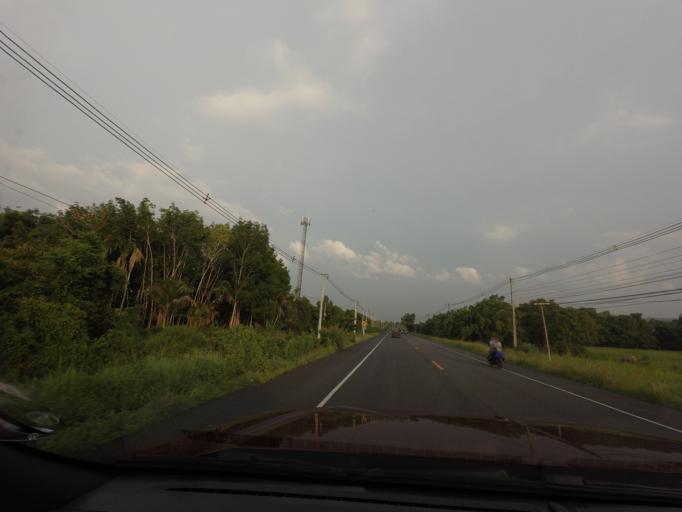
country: TH
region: Pattani
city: Mae Lan
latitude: 6.6447
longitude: 101.1820
